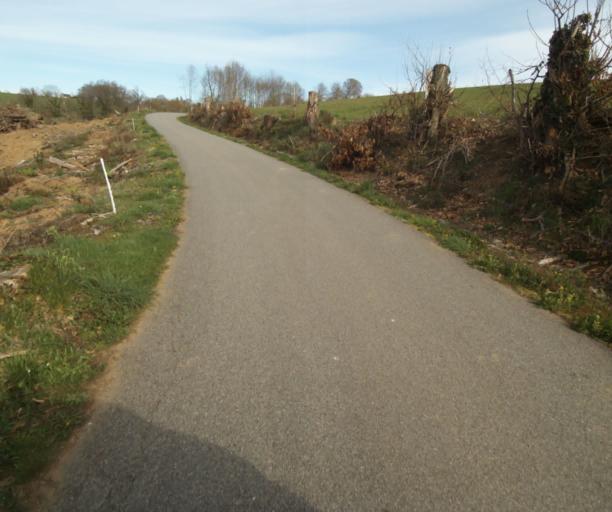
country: FR
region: Limousin
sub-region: Departement de la Correze
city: Chamboulive
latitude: 45.4179
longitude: 1.7901
